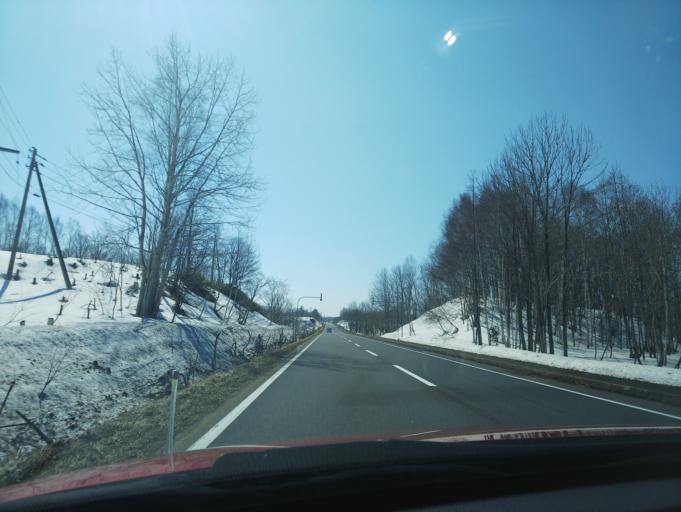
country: JP
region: Hokkaido
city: Nayoro
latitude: 44.6833
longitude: 142.2677
